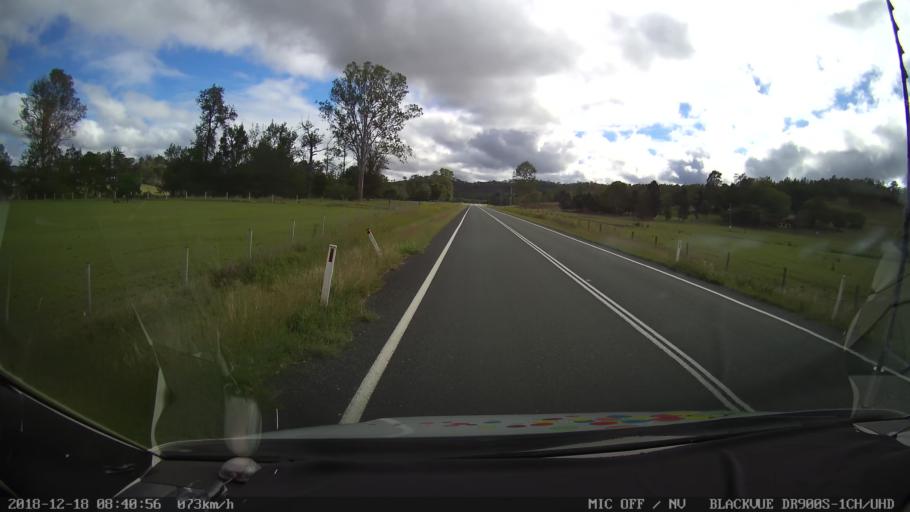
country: AU
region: Queensland
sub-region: Logan
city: Cedar Vale
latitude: -28.2403
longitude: 152.8523
